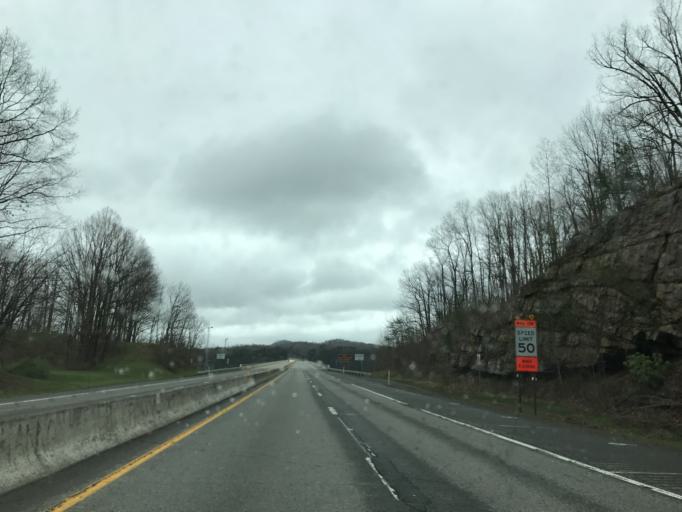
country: US
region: West Virginia
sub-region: Fayette County
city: Fayetteville
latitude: 38.0656
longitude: -81.0891
